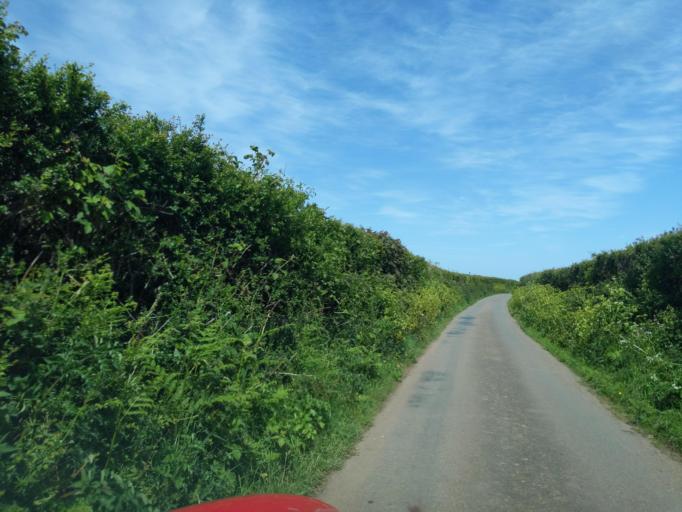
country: GB
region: England
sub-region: Borough of Torbay
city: Brixham
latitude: 50.3585
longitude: -3.5359
